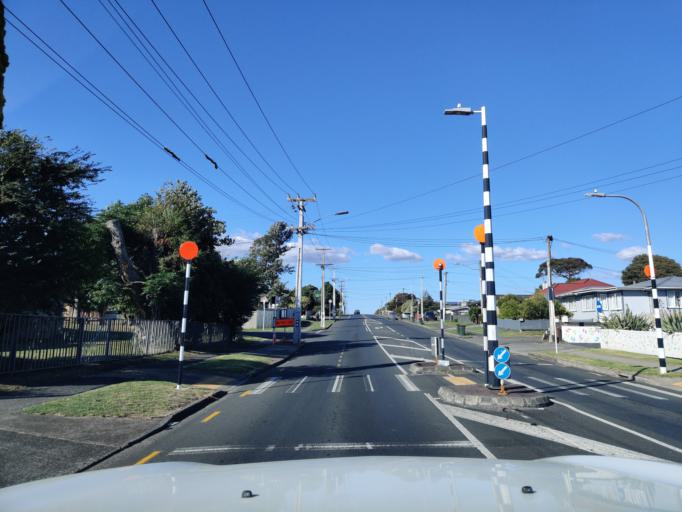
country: NZ
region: Auckland
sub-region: Auckland
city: Takanini
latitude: -37.0360
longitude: 174.8955
